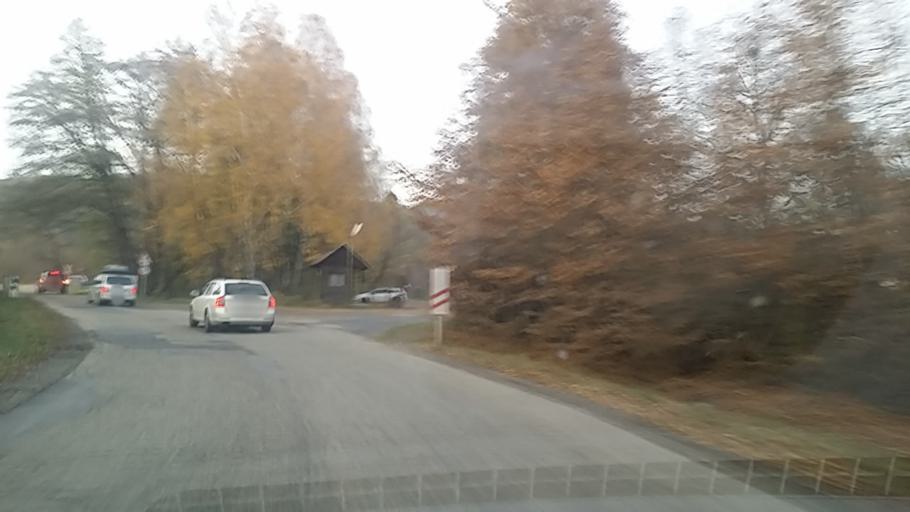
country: HU
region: Borsod-Abauj-Zemplen
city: Sarospatak
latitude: 48.4653
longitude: 21.4969
